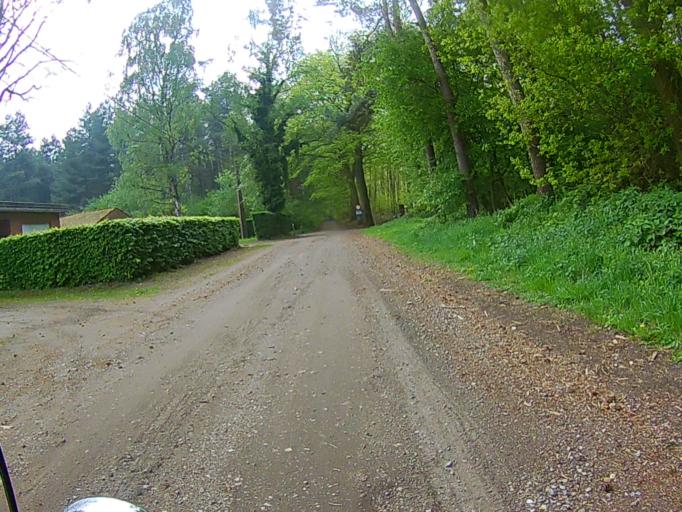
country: BE
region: Flanders
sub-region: Provincie Antwerpen
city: Grobbendonk
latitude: 51.2034
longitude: 4.7388
